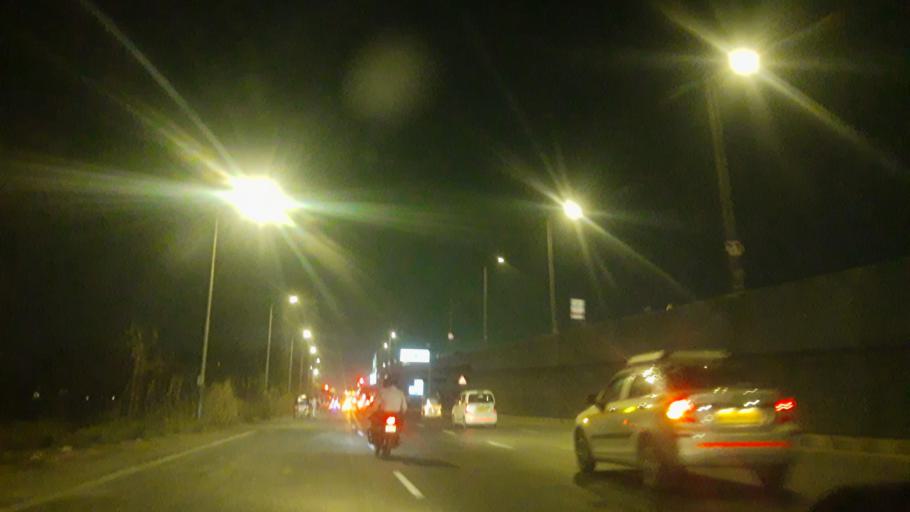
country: IN
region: Maharashtra
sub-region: Thane
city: Airoli
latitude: 19.1565
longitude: 72.9585
